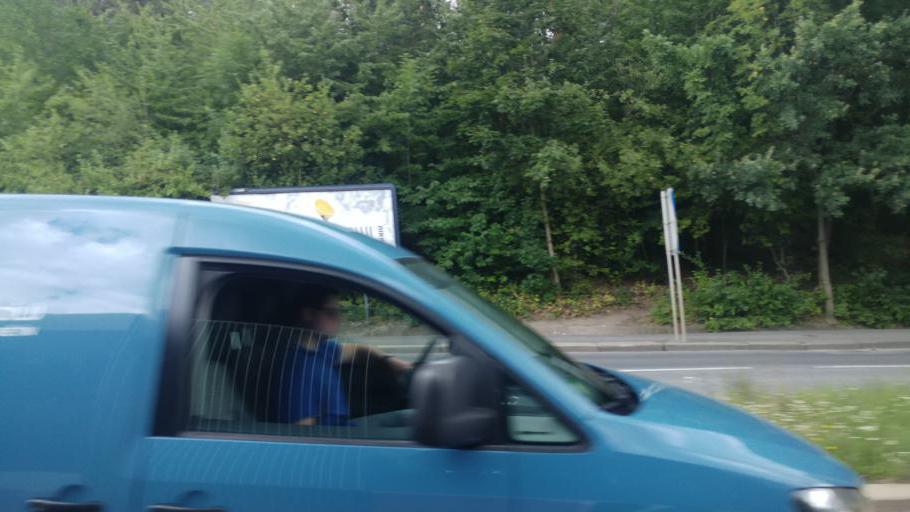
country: CZ
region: Praha
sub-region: Praha 9
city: Prosek
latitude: 50.0971
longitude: 14.4957
